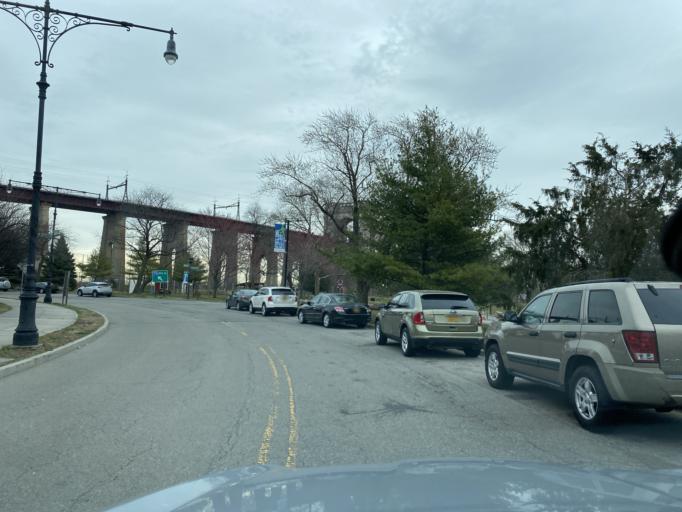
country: US
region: New York
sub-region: New York County
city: Manhattan
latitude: 40.7845
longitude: -73.9272
